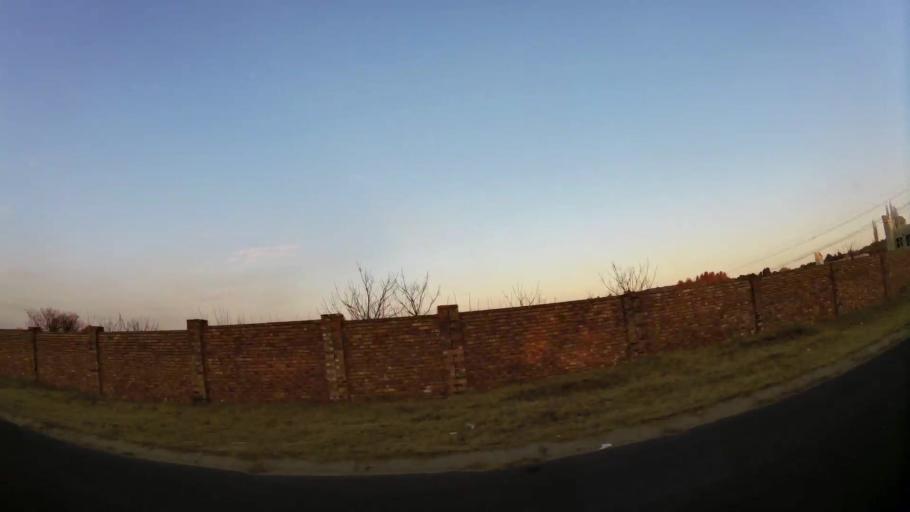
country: ZA
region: Gauteng
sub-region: City of Johannesburg Metropolitan Municipality
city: Diepsloot
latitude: -26.0218
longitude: 28.0331
